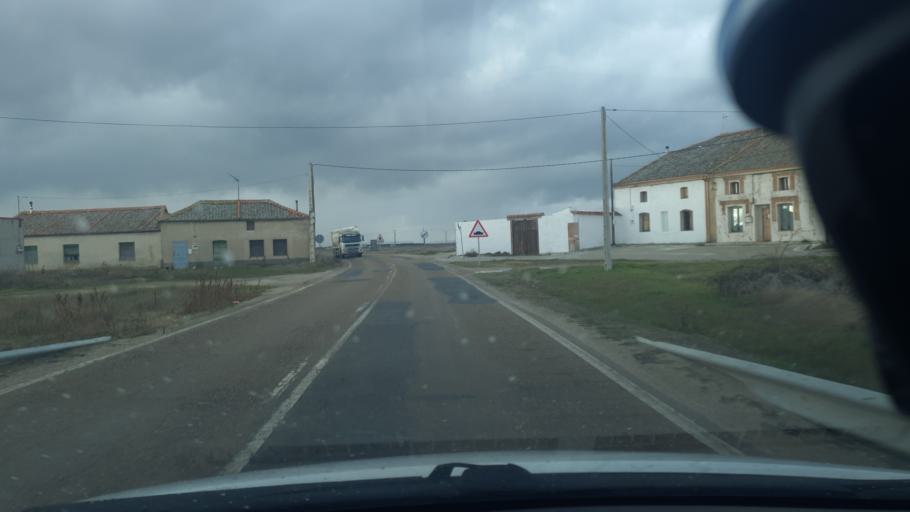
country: ES
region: Castille and Leon
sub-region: Provincia de Segovia
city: Sanchonuno
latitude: 41.3107
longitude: -4.3665
